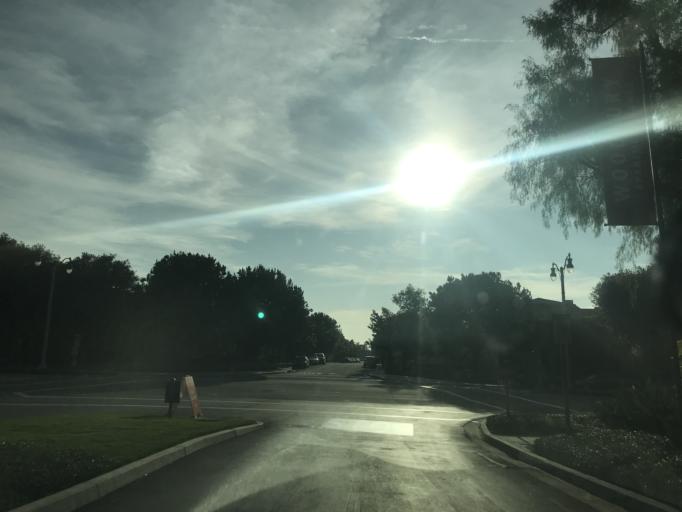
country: US
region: California
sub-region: Orange County
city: North Tustin
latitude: 33.7020
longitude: -117.7475
